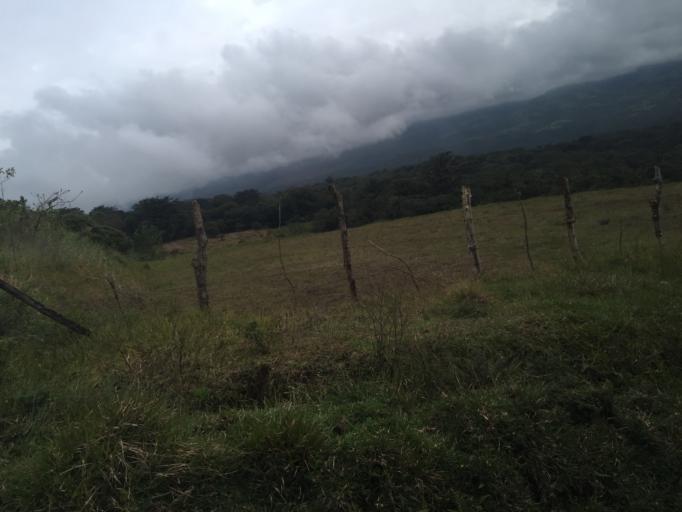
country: CR
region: Heredia
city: Angeles
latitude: 10.0414
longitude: -83.9888
